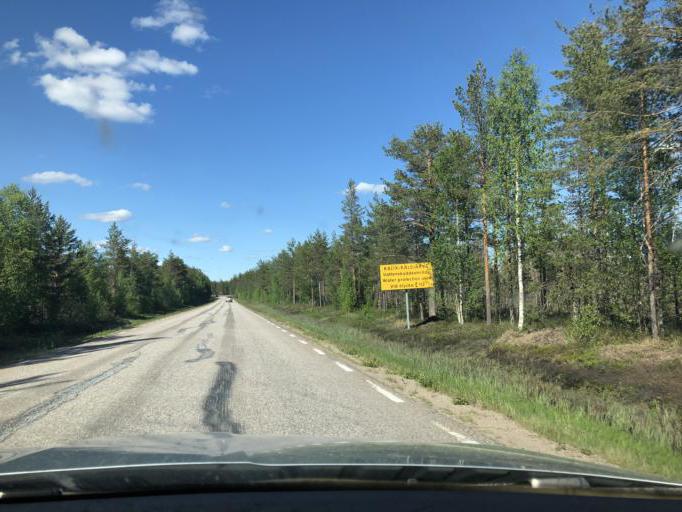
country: SE
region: Norrbotten
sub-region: Kalix Kommun
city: Kalix
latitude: 65.9013
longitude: 23.1702
